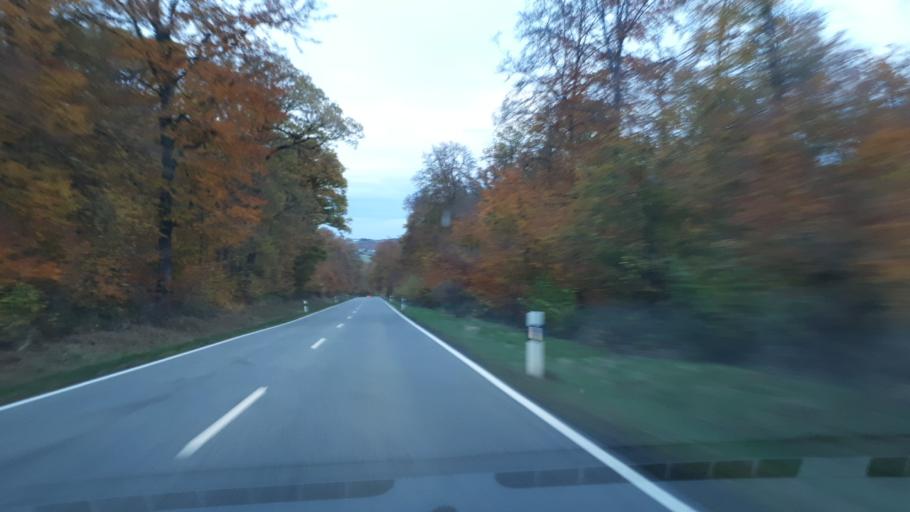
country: DE
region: Rheinland-Pfalz
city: Leienkaul
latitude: 50.1937
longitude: 7.0808
